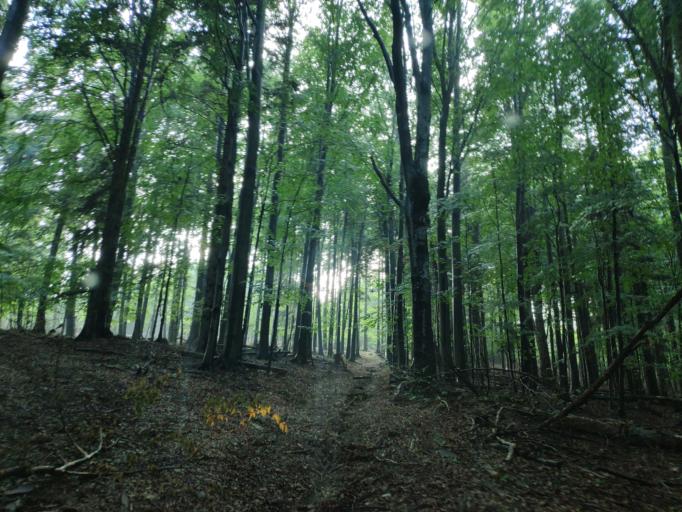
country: SK
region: Kosicky
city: Medzev
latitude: 48.7494
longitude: 20.9924
